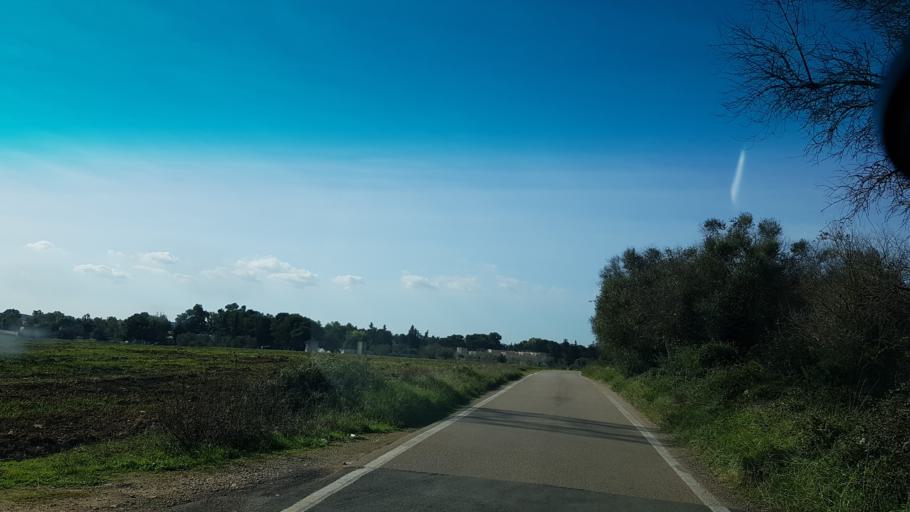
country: IT
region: Apulia
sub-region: Provincia di Lecce
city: Arnesano
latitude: 40.3501
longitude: 18.1214
